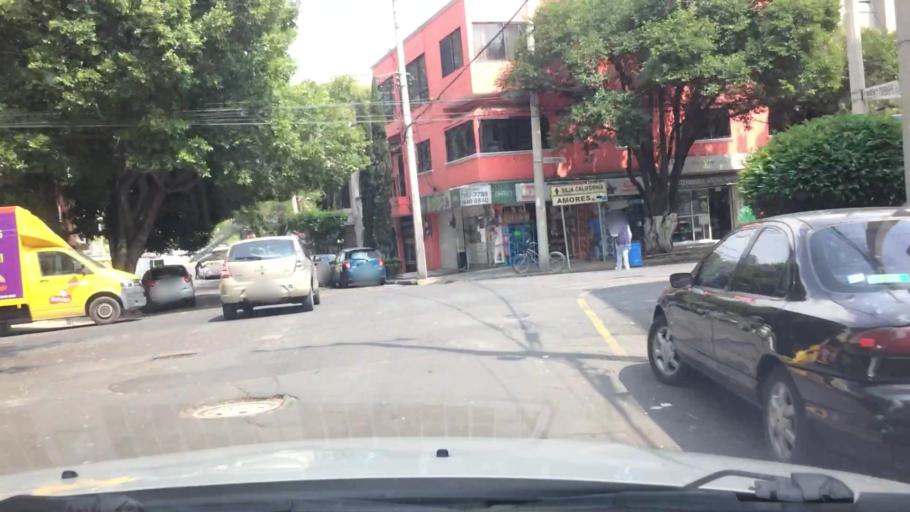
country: MX
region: Mexico City
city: Benito Juarez
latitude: 19.4009
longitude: -99.1637
